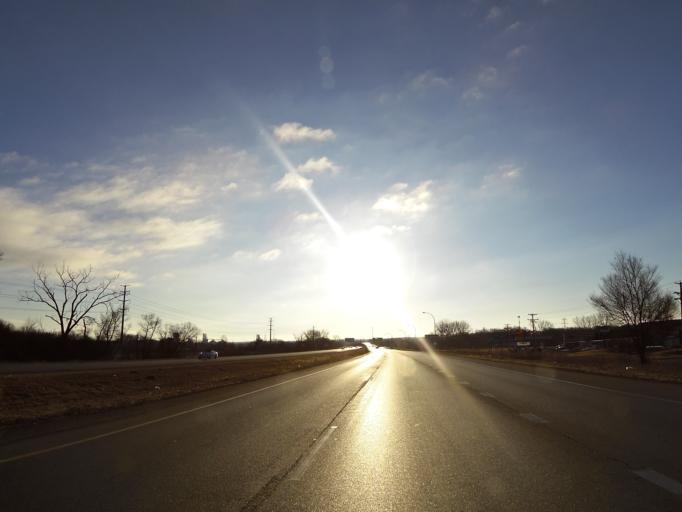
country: US
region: Minnesota
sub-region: Scott County
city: Savage
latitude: 44.7813
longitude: -93.3898
